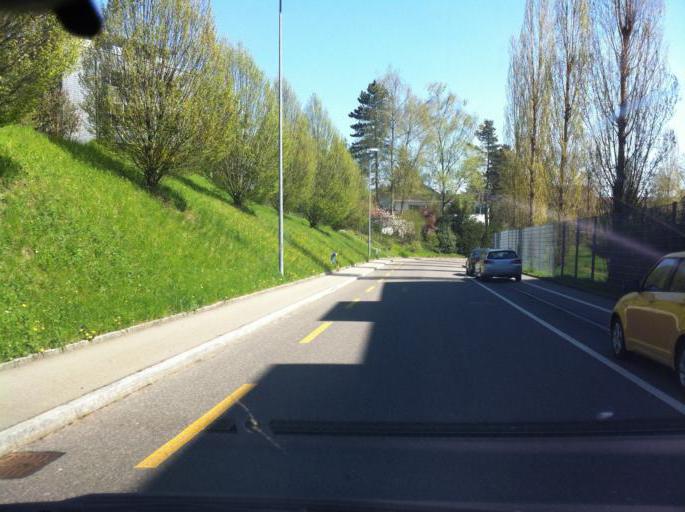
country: CH
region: Schaffhausen
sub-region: Bezirk Schaffhausen
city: Schaffhausen
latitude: 47.7136
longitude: 8.6406
